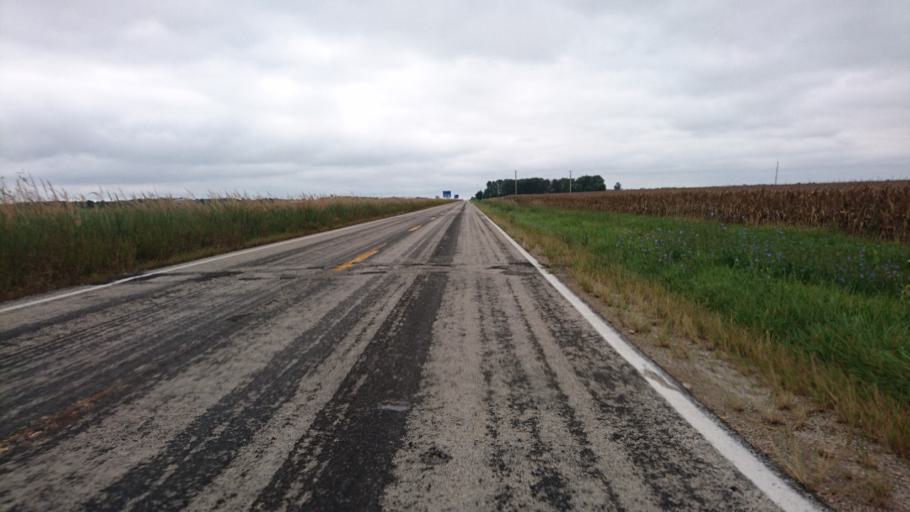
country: US
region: Illinois
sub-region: Montgomery County
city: Raymond
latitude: 39.3092
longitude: -89.6429
